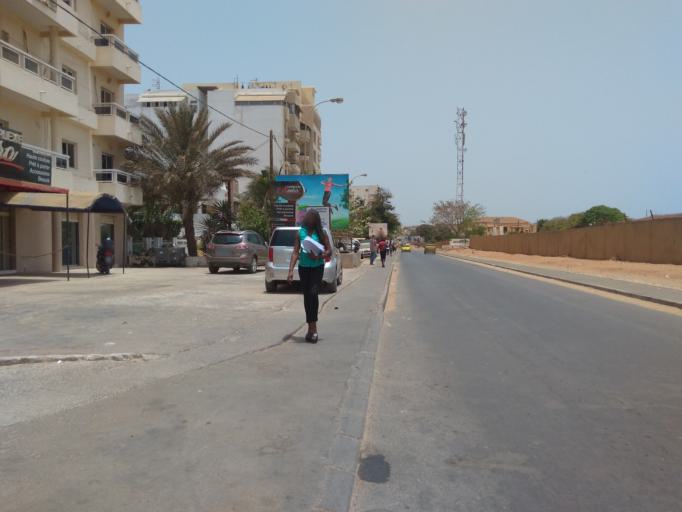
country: SN
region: Dakar
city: Grand Dakar
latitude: 14.7308
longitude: -17.4672
